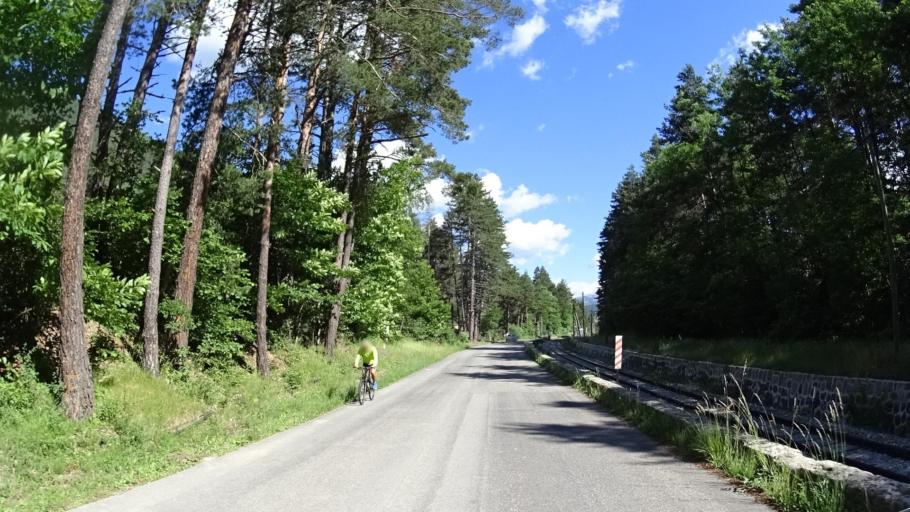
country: FR
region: Provence-Alpes-Cote d'Azur
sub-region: Departement des Alpes-de-Haute-Provence
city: Annot
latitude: 43.9845
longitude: 6.6490
